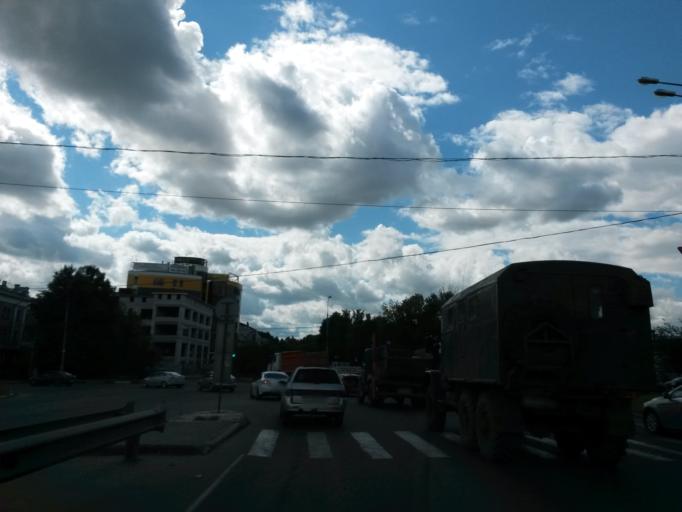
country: RU
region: Jaroslavl
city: Yaroslavl
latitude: 57.6091
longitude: 39.8602
